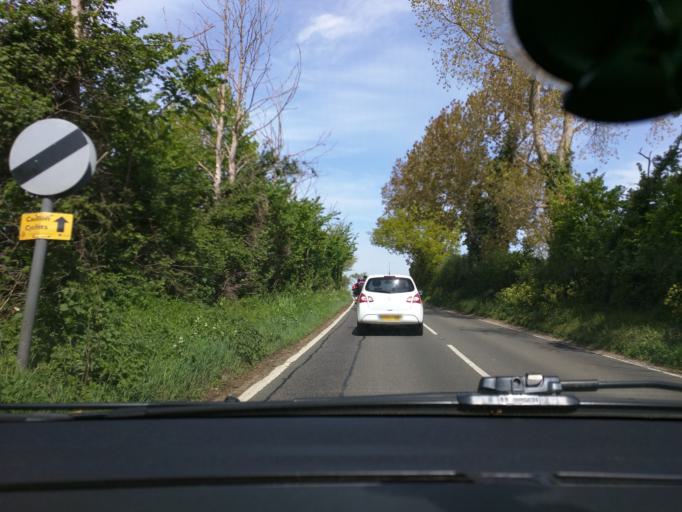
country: GB
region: England
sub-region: Suffolk
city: Leiston
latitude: 52.2406
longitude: 1.5662
